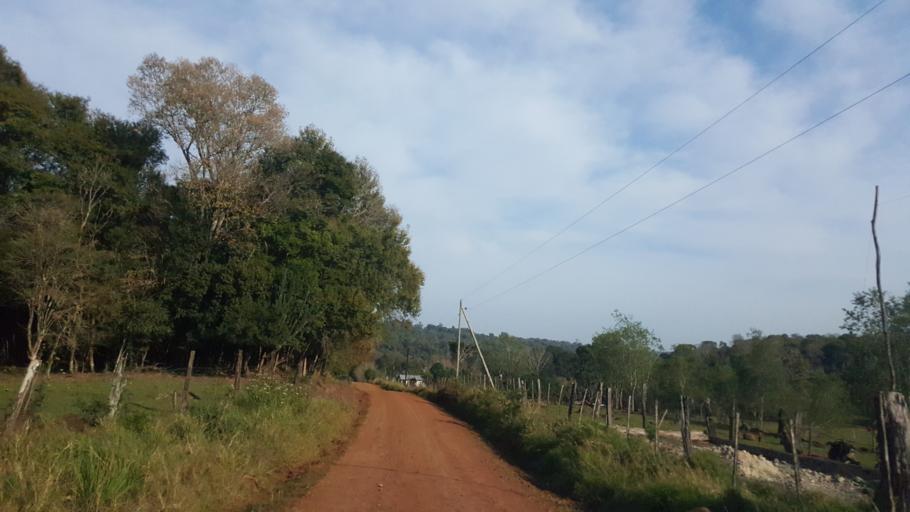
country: AR
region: Misiones
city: Capiovi
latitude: -26.9153
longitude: -55.0789
